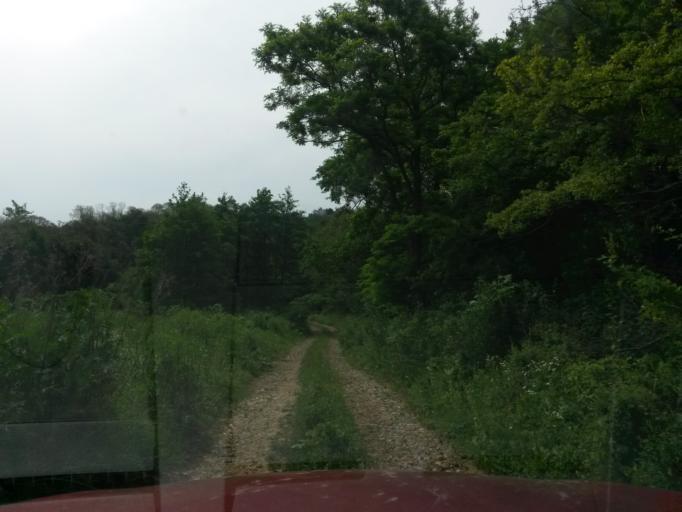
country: SK
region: Kosicky
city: Moldava nad Bodvou
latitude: 48.6661
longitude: 21.1273
